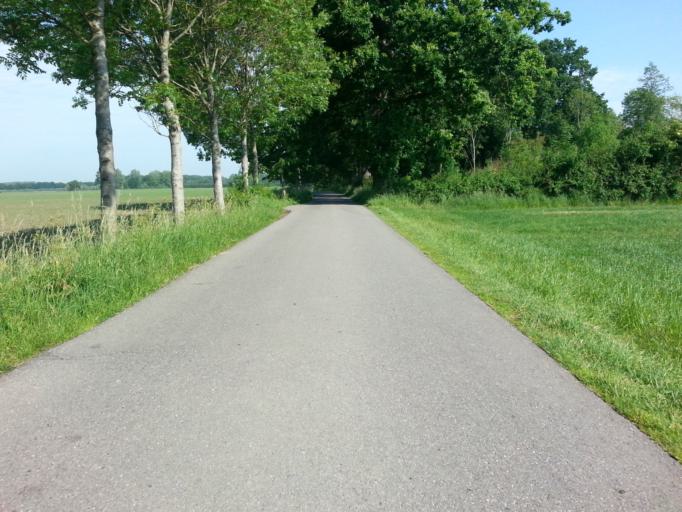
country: NL
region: Utrecht
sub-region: Gemeente Utrechtse Heuvelrug
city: Driebergen-Rijsenburg
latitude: 52.0237
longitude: 5.2641
